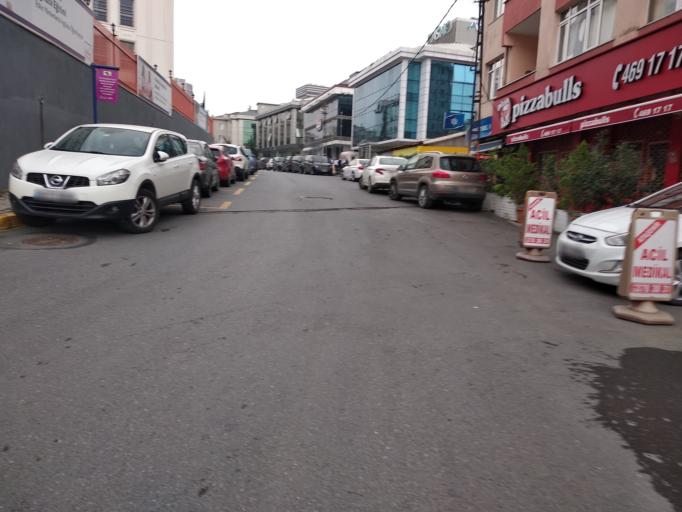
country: TR
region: Istanbul
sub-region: Atasehir
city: Atasehir
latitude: 40.9846
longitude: 29.1109
